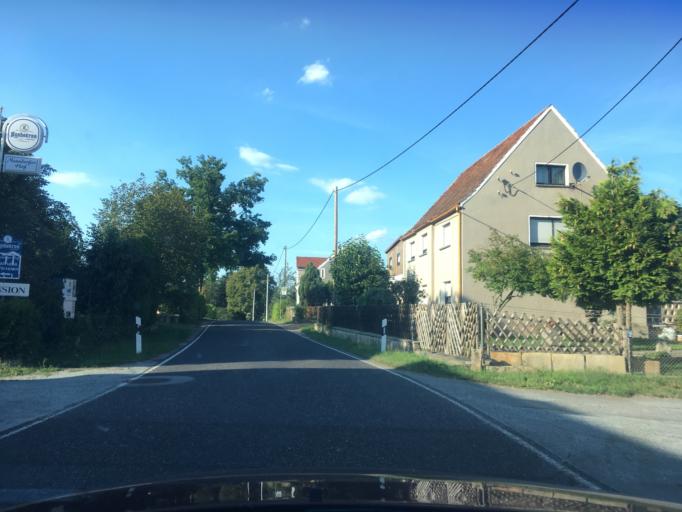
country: PL
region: Lower Silesian Voivodeship
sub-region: Powiat zgorzelecki
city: Piensk
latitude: 51.2128
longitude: 15.0022
